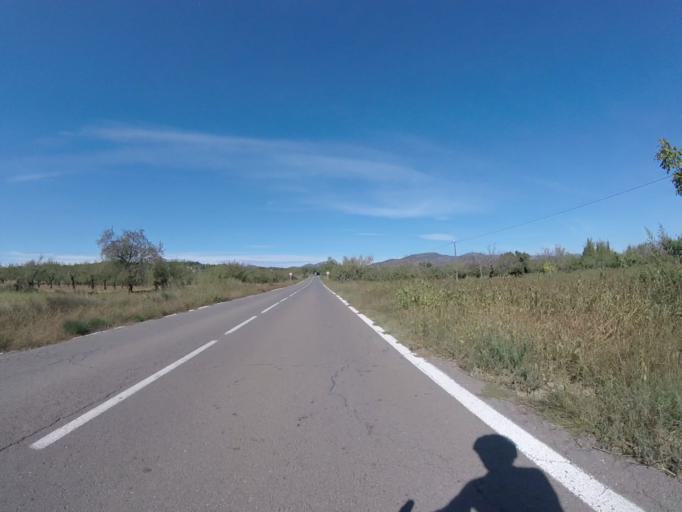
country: ES
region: Valencia
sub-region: Provincia de Castello
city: Benlloch
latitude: 40.2184
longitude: 0.0167
